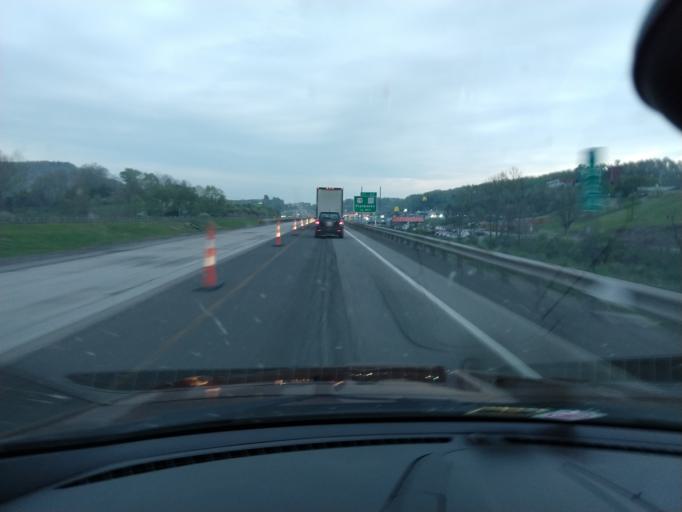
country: US
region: West Virginia
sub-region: Braxton County
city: Sutton
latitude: 38.6958
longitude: -80.6698
